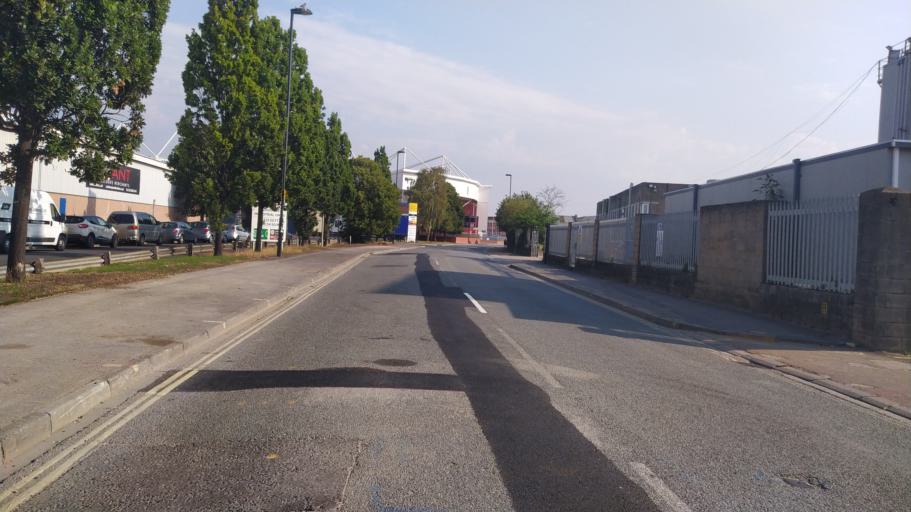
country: GB
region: England
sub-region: Southampton
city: Southampton
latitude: 50.9033
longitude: -1.3906
